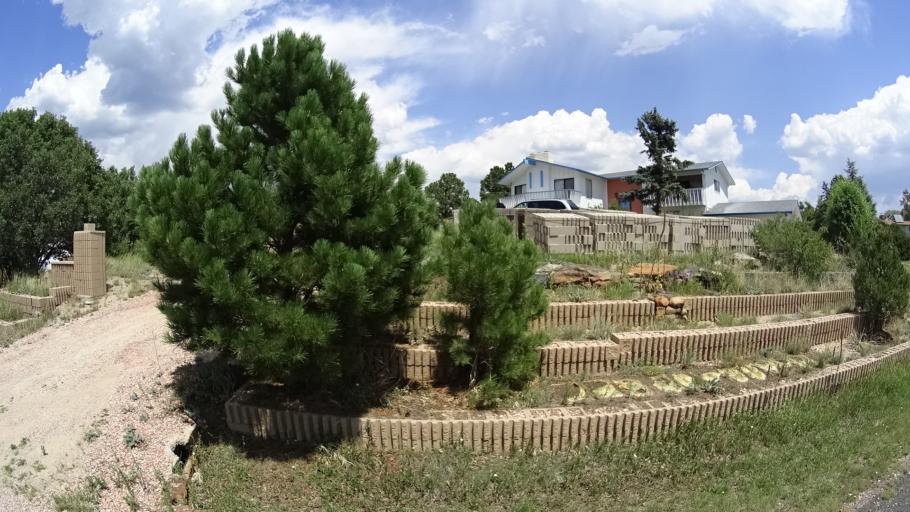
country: US
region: Colorado
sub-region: El Paso County
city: Air Force Academy
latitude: 38.9395
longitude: -104.8087
